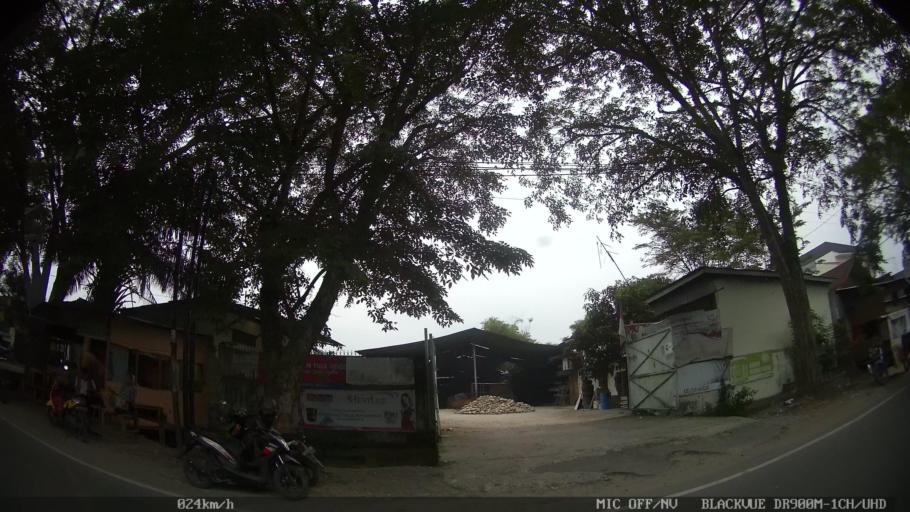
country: ID
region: North Sumatra
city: Medan
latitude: 3.5684
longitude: 98.7084
